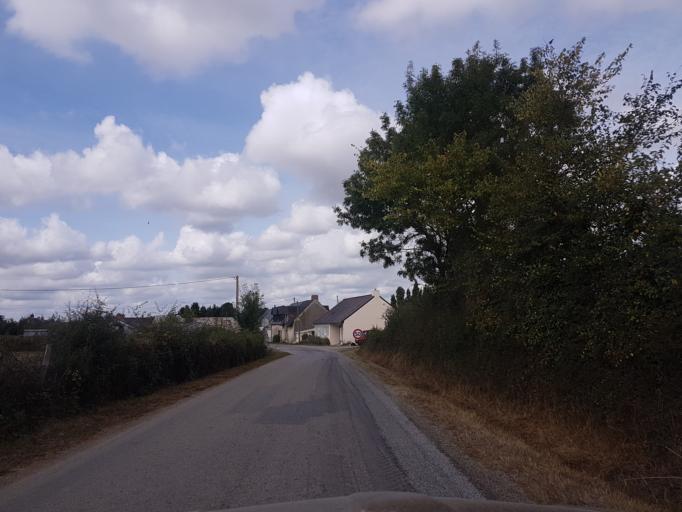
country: FR
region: Pays de la Loire
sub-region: Departement de la Loire-Atlantique
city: Petit-Mars
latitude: 47.4110
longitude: -1.4371
